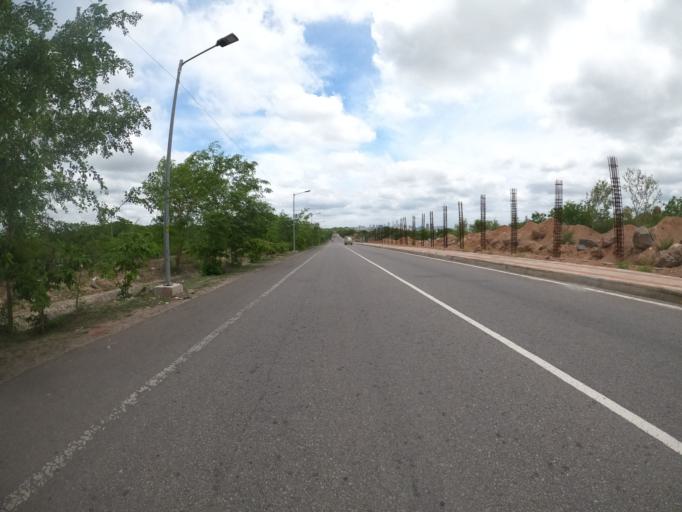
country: IN
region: Telangana
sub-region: Hyderabad
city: Hyderabad
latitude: 17.3656
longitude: 78.3527
